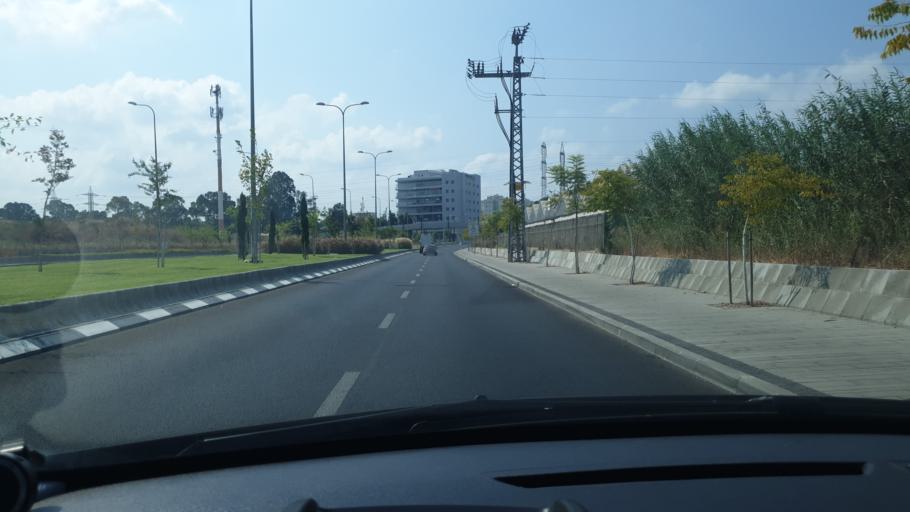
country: IL
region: Haifa
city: Qiryat Bialik
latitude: 32.8154
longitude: 35.0831
